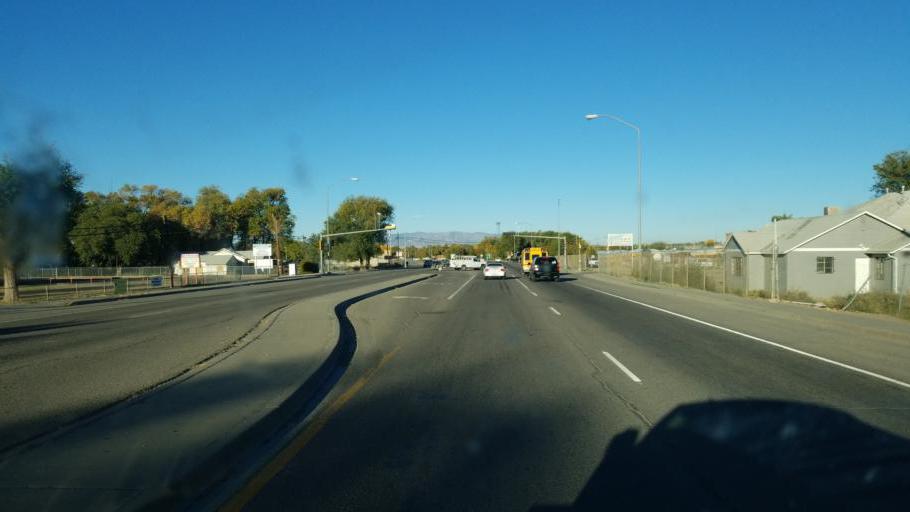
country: US
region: New Mexico
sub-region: San Juan County
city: Shiprock
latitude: 36.7851
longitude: -108.6795
